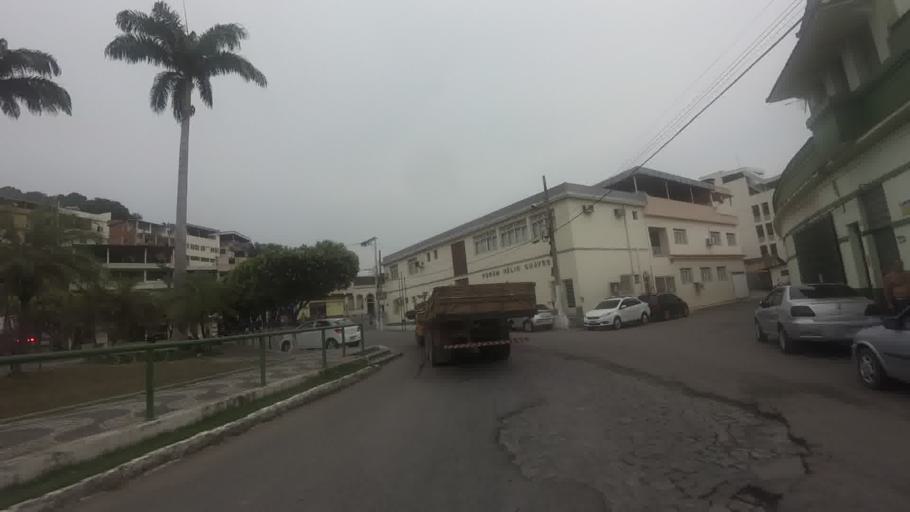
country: BR
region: Minas Gerais
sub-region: Recreio
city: Recreio
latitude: -21.6585
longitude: -42.3444
